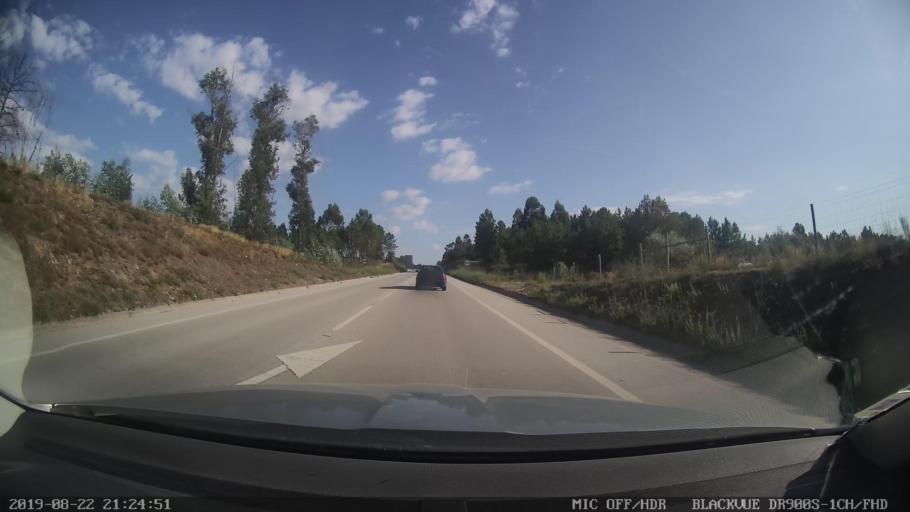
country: PT
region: Castelo Branco
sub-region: Serta
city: Serta
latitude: 39.8461
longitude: -8.1242
